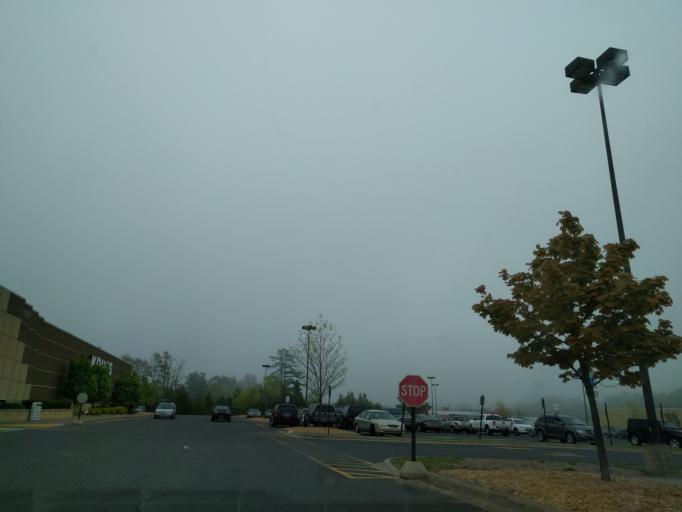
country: US
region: Michigan
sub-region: Marquette County
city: Trowbridge Park
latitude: 46.5508
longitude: -87.4515
